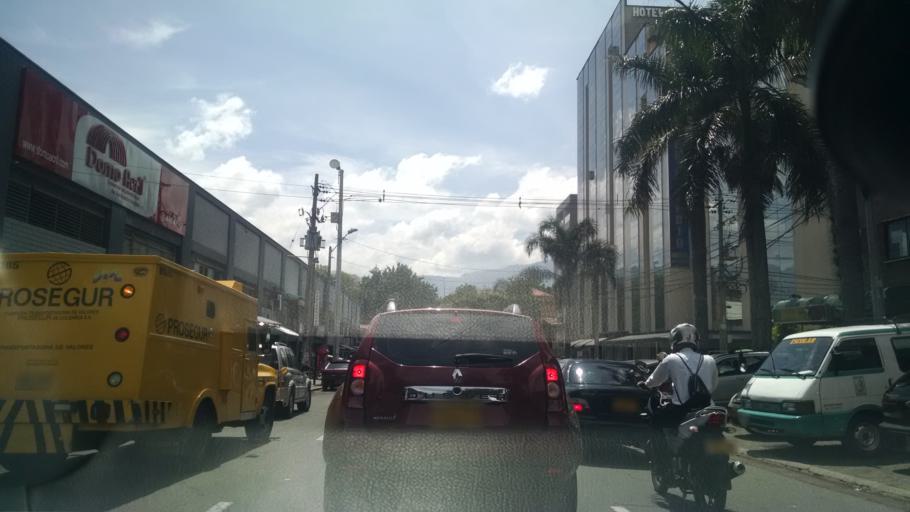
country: CO
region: Antioquia
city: Medellin
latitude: 6.2577
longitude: -75.5857
